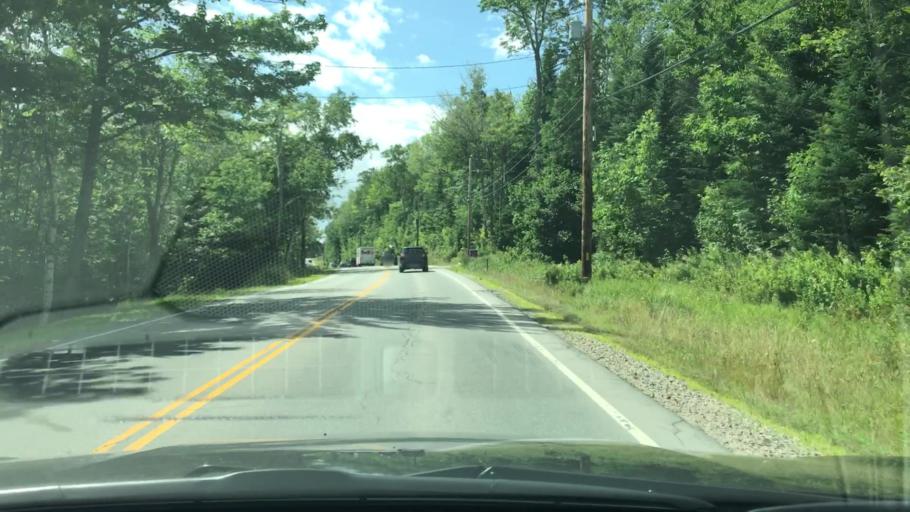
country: US
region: New Hampshire
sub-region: Coos County
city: Jefferson
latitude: 44.3616
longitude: -71.3787
